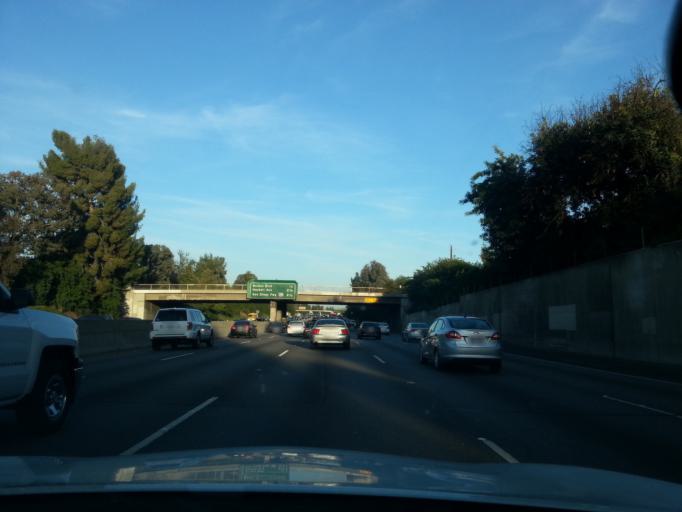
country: US
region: California
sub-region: Los Angeles County
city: Northridge
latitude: 34.1711
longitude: -118.5110
